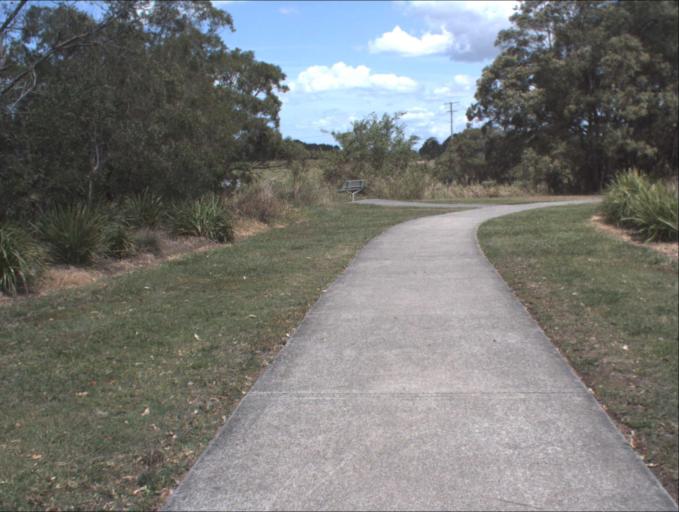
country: AU
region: Queensland
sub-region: Logan
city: Slacks Creek
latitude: -27.6709
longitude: 153.1597
